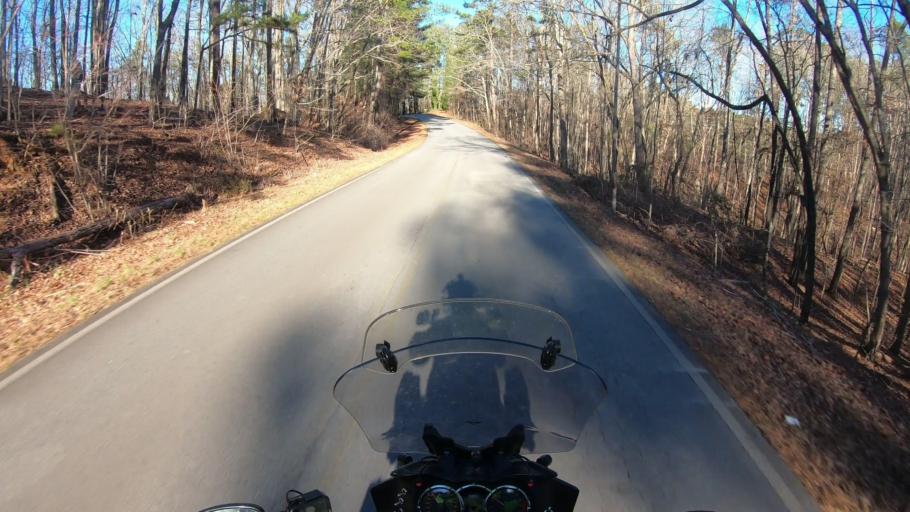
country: US
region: Georgia
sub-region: Haralson County
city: Tallapoosa
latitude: 33.8660
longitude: -85.3407
